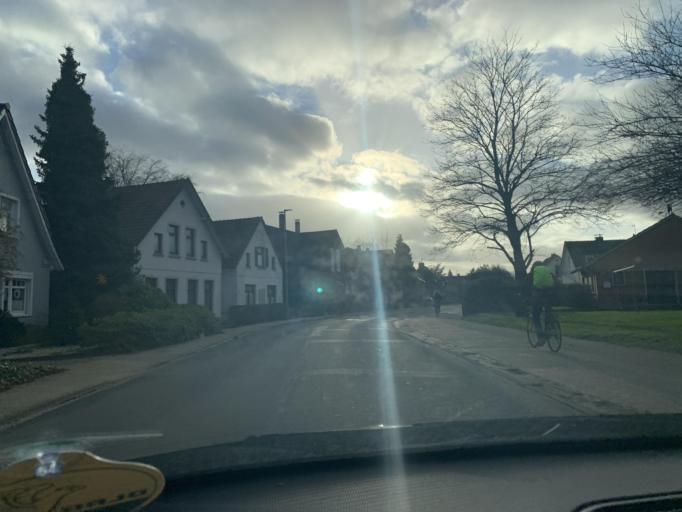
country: DE
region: Lower Saxony
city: Varel
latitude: 53.3896
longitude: 8.1454
